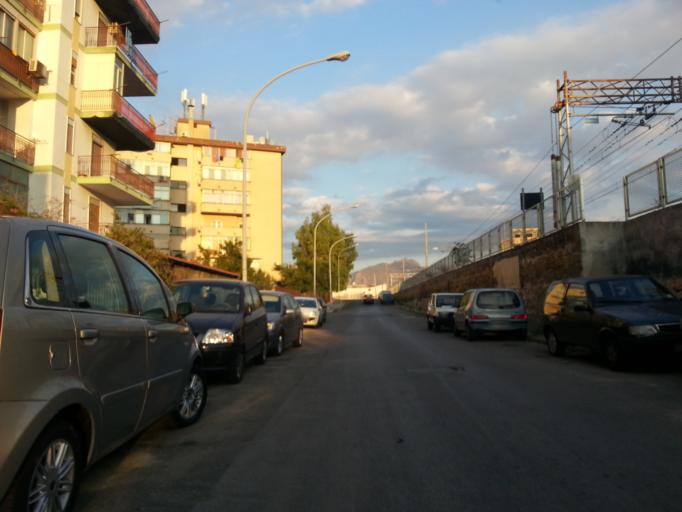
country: IT
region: Sicily
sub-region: Palermo
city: Ciaculli
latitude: 38.0997
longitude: 13.3820
